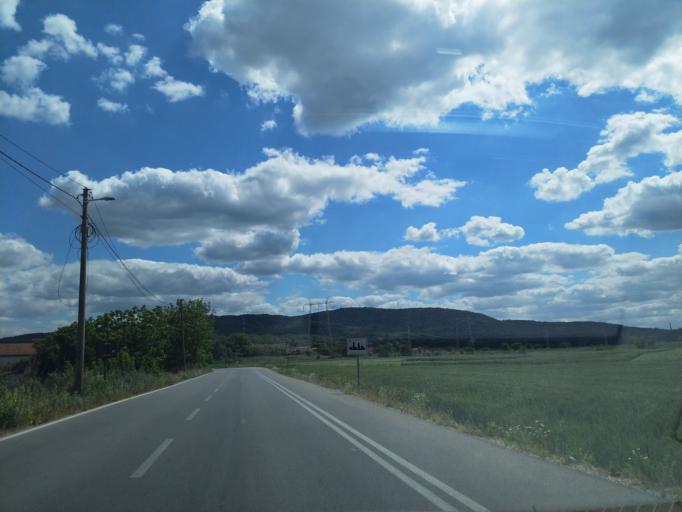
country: RS
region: Central Serbia
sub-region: Pomoravski Okrug
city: Jagodina
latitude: 43.9542
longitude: 21.2909
